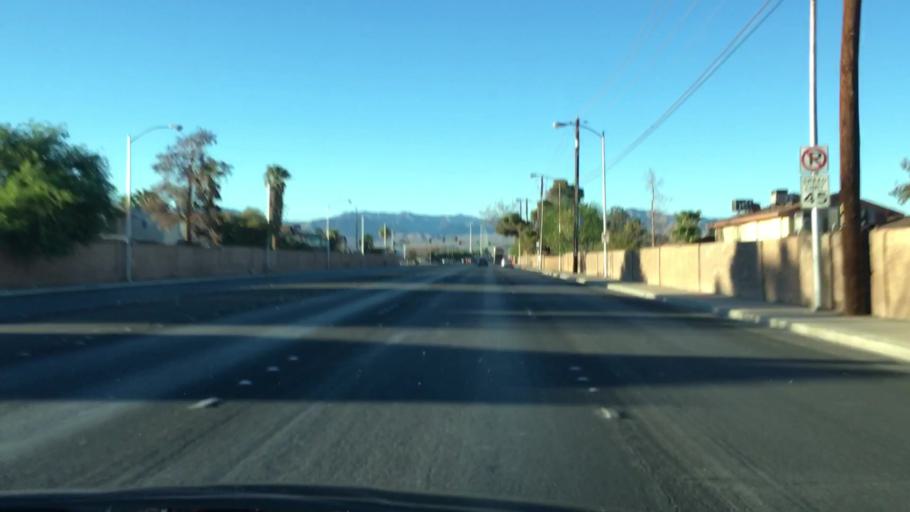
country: US
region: Nevada
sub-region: Clark County
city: Sunrise Manor
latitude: 36.2305
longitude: -115.0801
